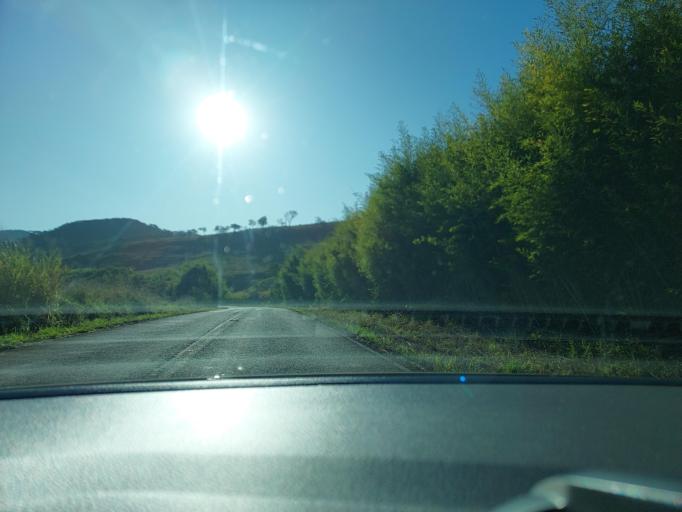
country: BR
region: Minas Gerais
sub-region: Alvinopolis
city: Alvinopolis
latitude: -20.2040
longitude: -42.9241
